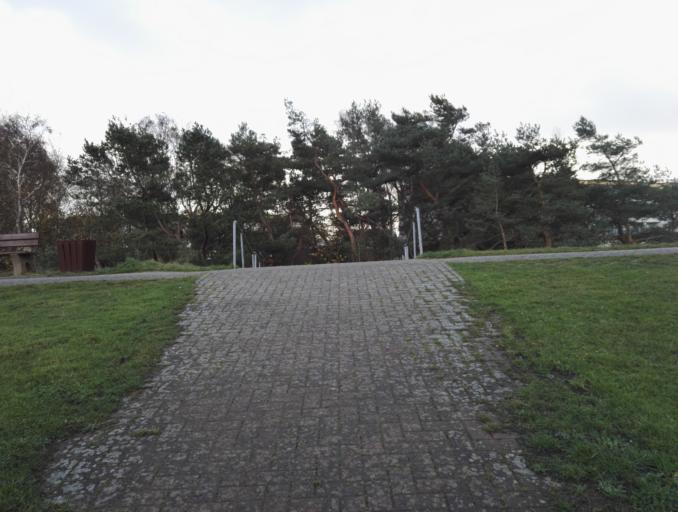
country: DE
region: Schleswig-Holstein
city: Wangels
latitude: 54.3105
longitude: 10.7916
